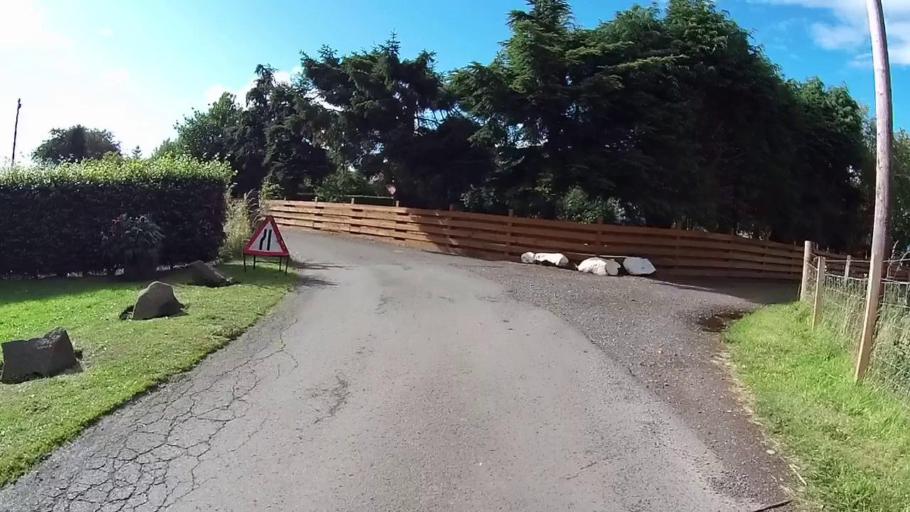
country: GB
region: Scotland
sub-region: Fife
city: Ladybank
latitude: 56.2869
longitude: -3.1537
